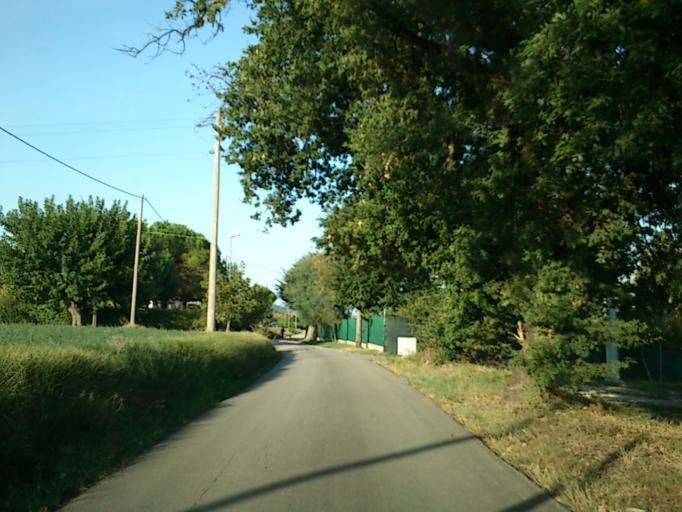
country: IT
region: The Marches
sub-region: Provincia di Pesaro e Urbino
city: Calcinelli
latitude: 43.7678
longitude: 12.9223
